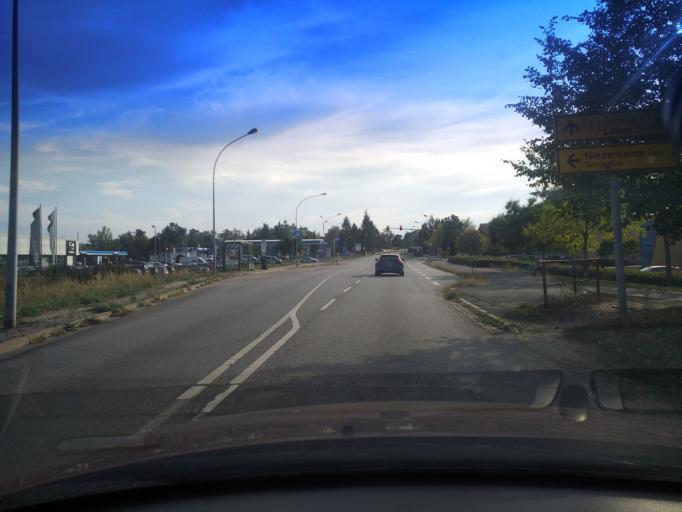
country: DE
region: Saxony
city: Bautzen
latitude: 51.1915
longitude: 14.4522
